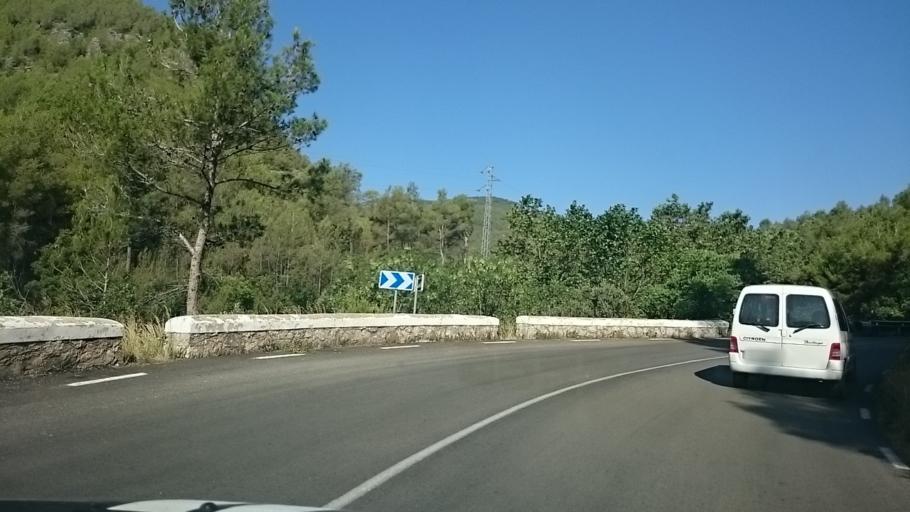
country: ES
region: Catalonia
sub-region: Provincia de Barcelona
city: Sant Marti Sarroca
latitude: 41.4000
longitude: 1.5421
